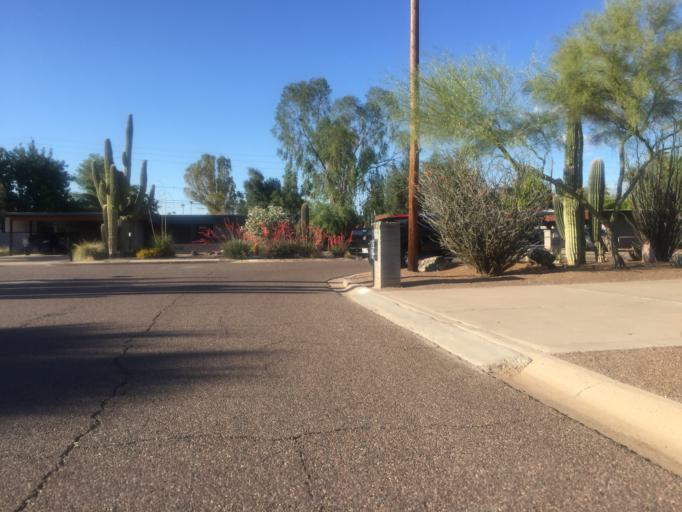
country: US
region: Arizona
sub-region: Maricopa County
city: Paradise Valley
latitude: 33.5784
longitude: -112.0056
